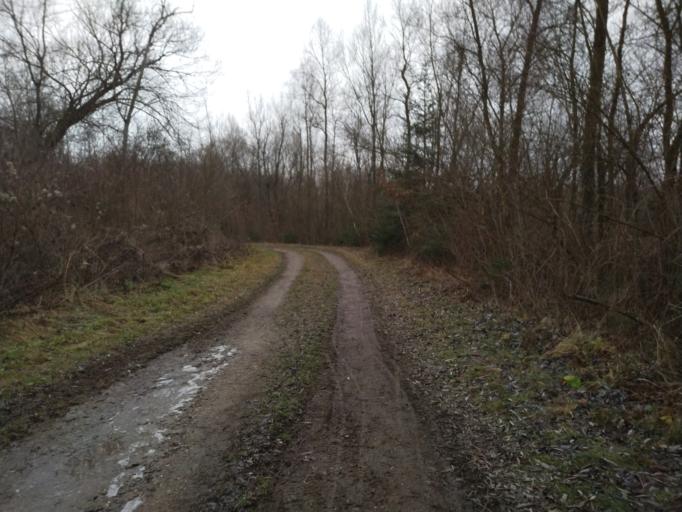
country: DE
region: Bavaria
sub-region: Swabia
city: Rettenbach
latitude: 48.4775
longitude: 10.3145
